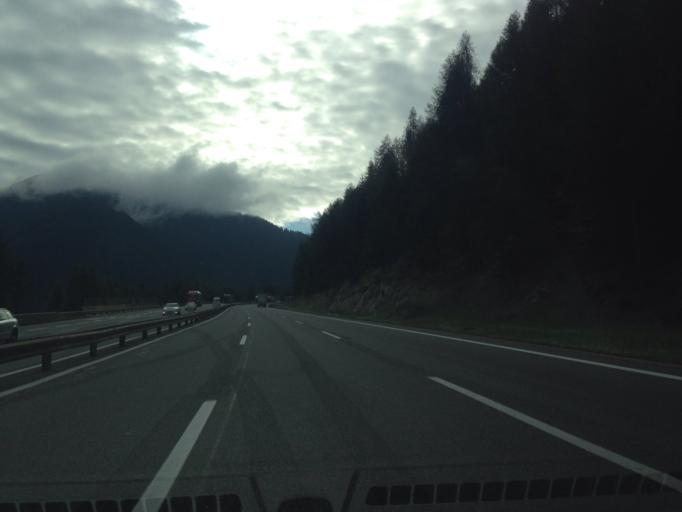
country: AT
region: Tyrol
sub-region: Politischer Bezirk Innsbruck Land
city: Steinach am Brenner
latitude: 47.0835
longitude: 11.4627
